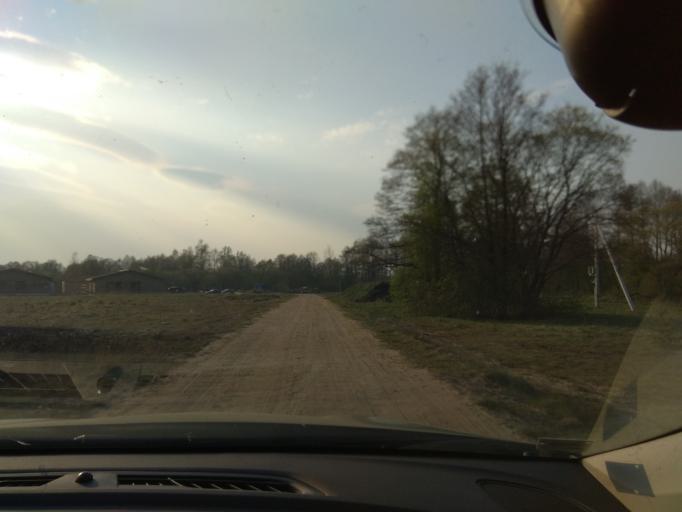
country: LT
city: Baltoji Voke
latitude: 54.5945
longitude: 25.1885
